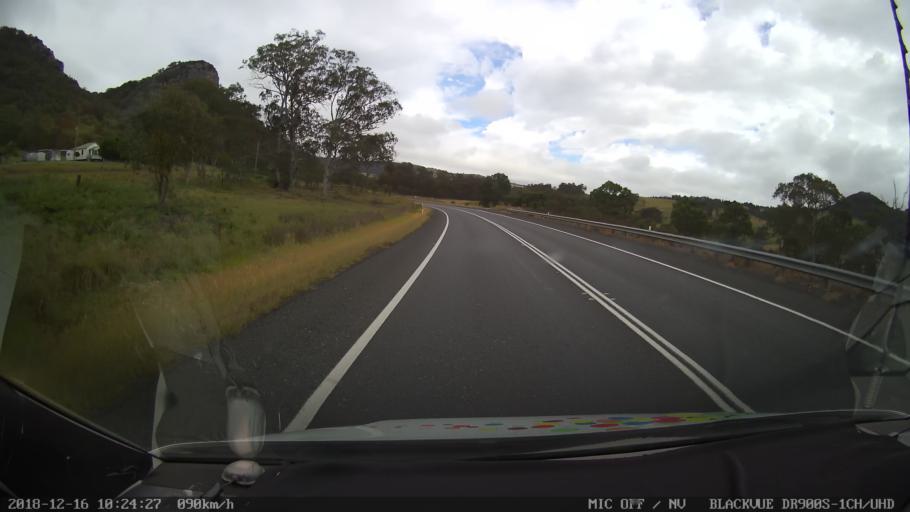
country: AU
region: New South Wales
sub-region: Tenterfield Municipality
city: Carrolls Creek
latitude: -29.1701
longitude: 152.0071
